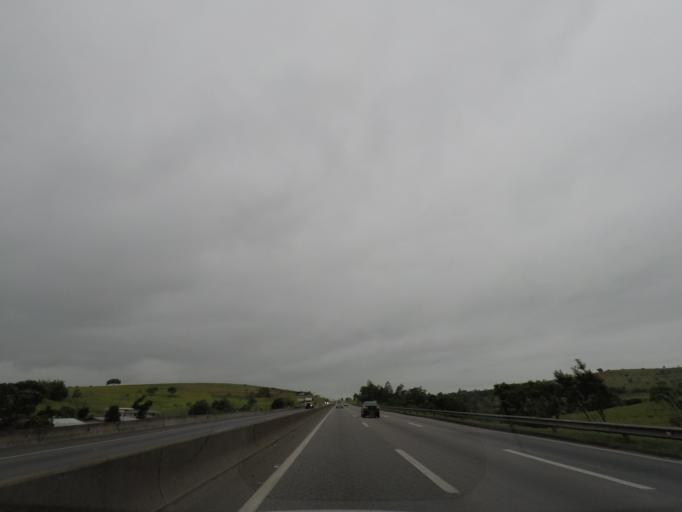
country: BR
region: Sao Paulo
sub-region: Tremembe
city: Tremembe
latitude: -22.9947
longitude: -45.4892
